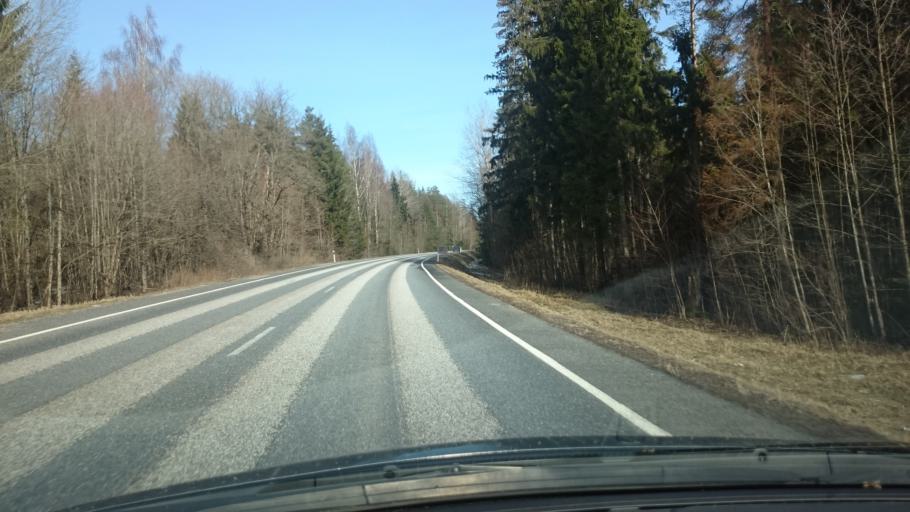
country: EE
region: Jaervamaa
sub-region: Tueri vald
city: Sarevere
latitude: 58.7410
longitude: 25.3029
